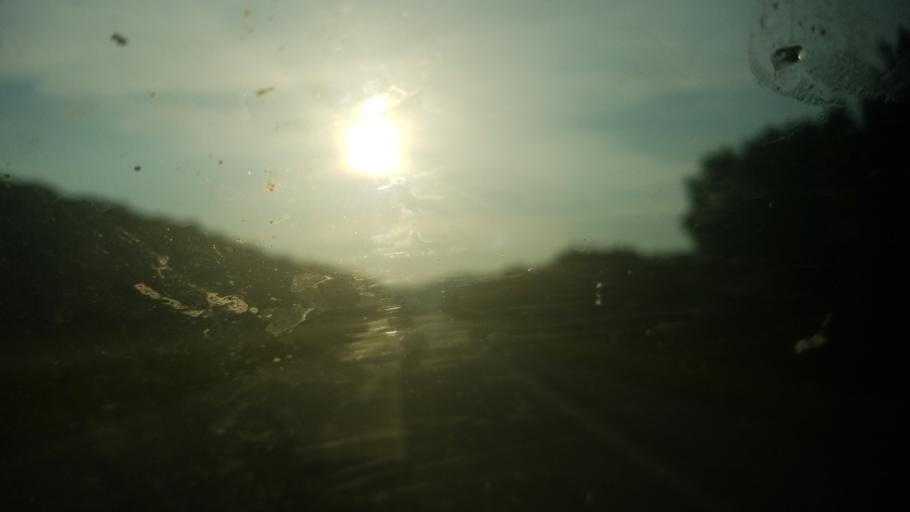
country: US
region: Ohio
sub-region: Pike County
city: Piketon
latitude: 39.0442
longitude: -83.1707
